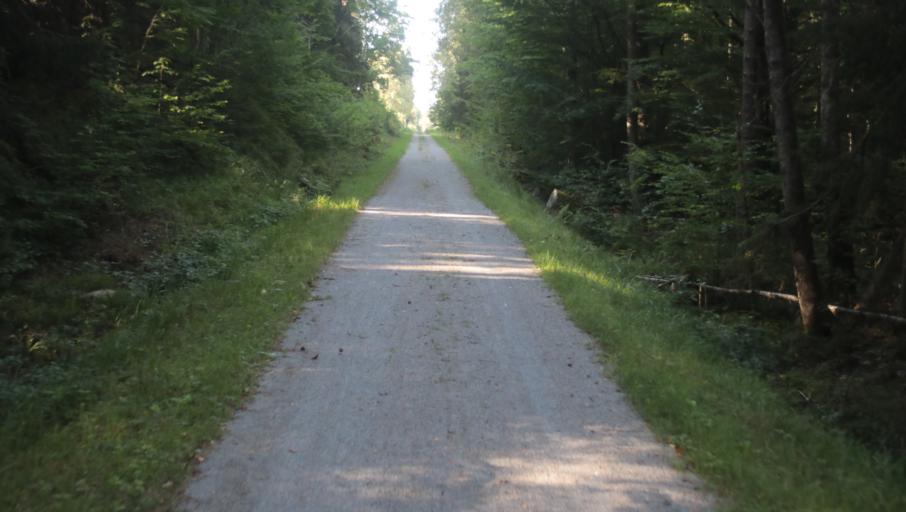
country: SE
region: Blekinge
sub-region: Karlshamns Kommun
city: Svangsta
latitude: 56.3539
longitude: 14.6929
